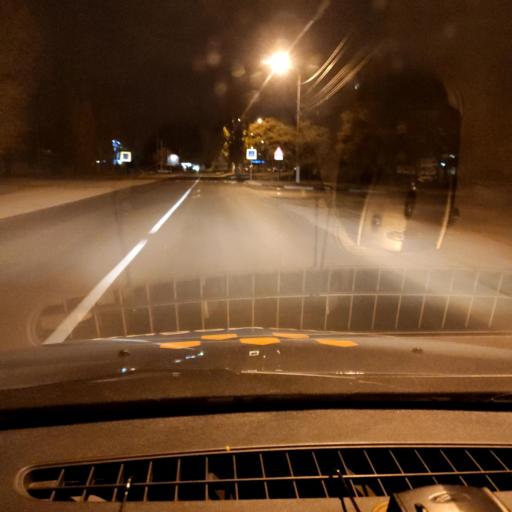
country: RU
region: Voronezj
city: Shilovo
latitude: 51.5501
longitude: 39.0877
